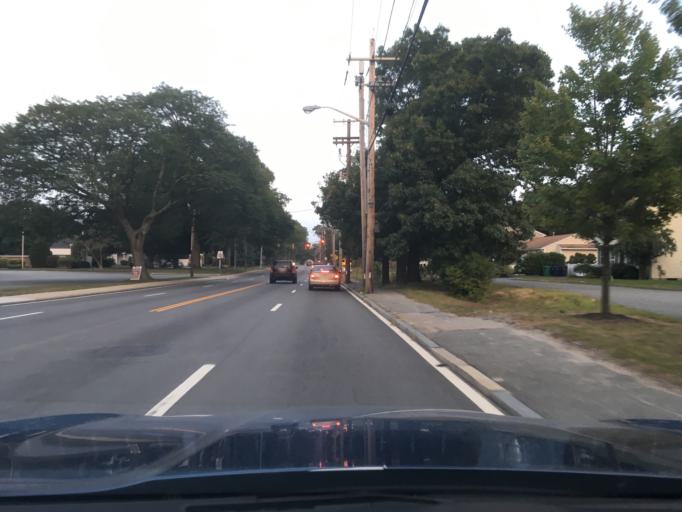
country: US
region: Rhode Island
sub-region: Kent County
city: Warwick
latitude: 41.7072
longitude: -71.4330
